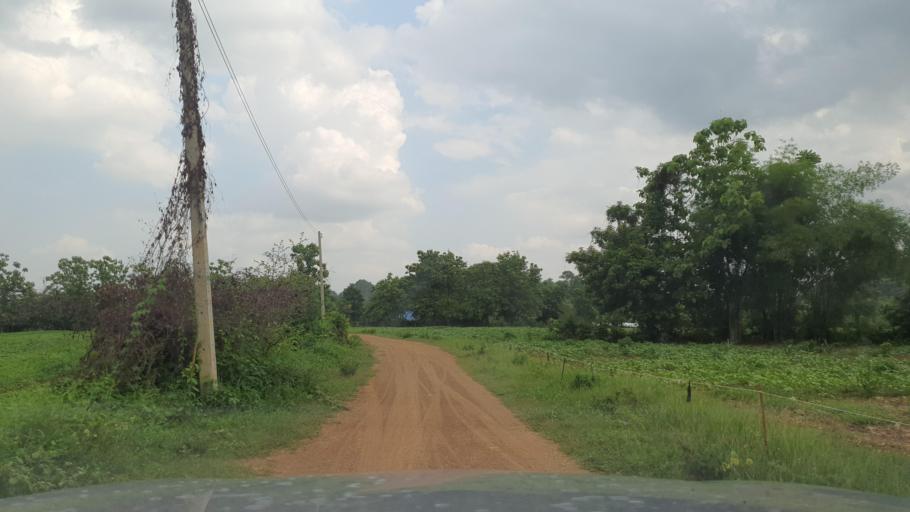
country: TH
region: Sukhothai
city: Thung Saliam
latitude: 17.2474
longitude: 99.5439
